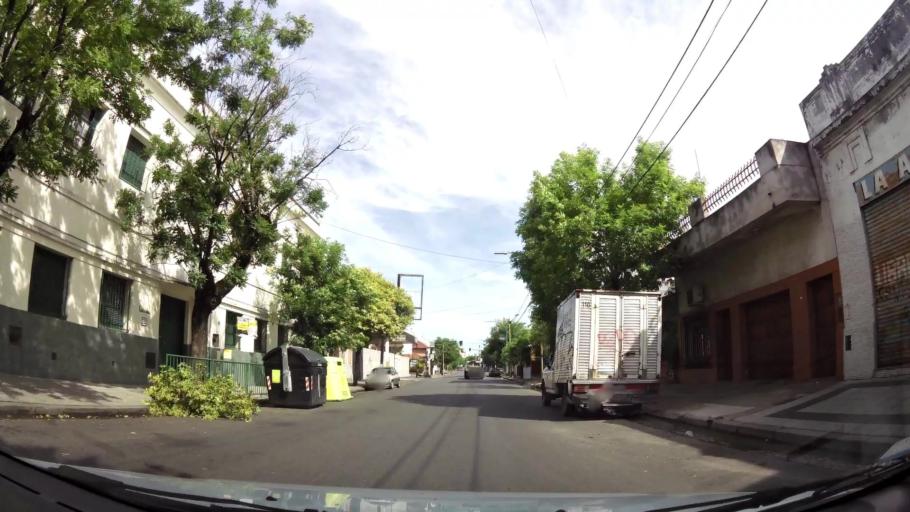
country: AR
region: Buenos Aires F.D.
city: Villa Lugano
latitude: -34.6666
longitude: -58.5023
